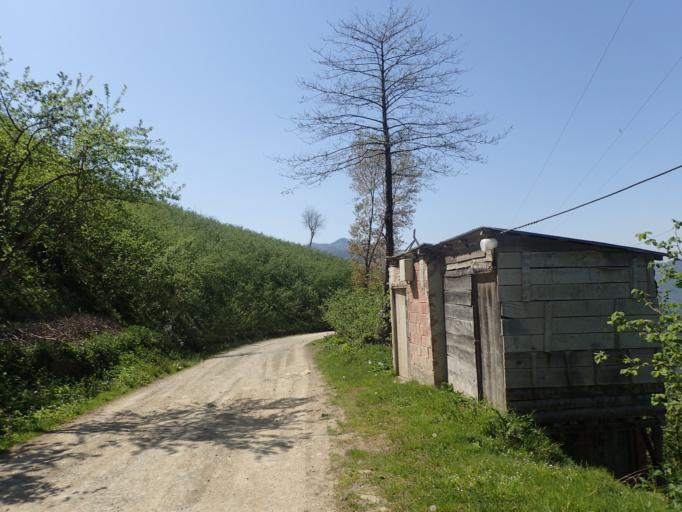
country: TR
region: Ordu
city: Kabaduz
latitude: 40.7464
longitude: 37.8899
